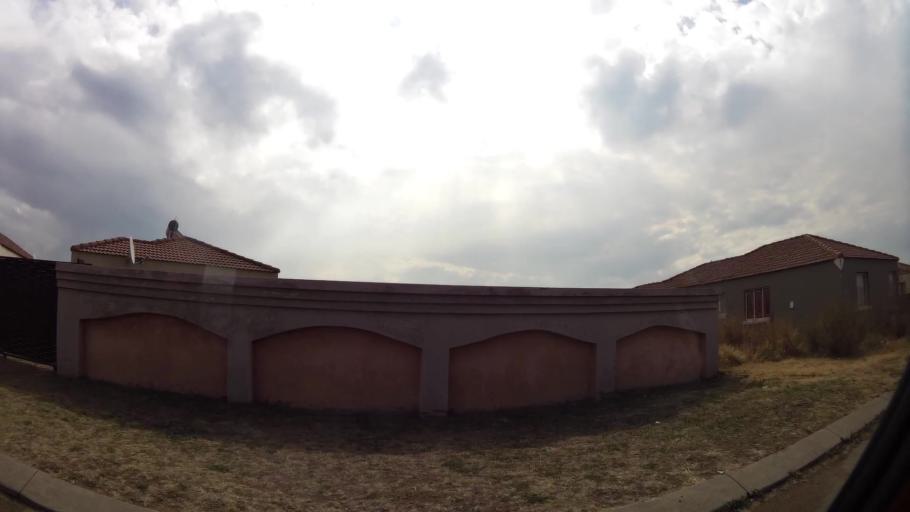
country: ZA
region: Gauteng
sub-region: Sedibeng District Municipality
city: Vanderbijlpark
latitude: -26.7147
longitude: 27.8855
